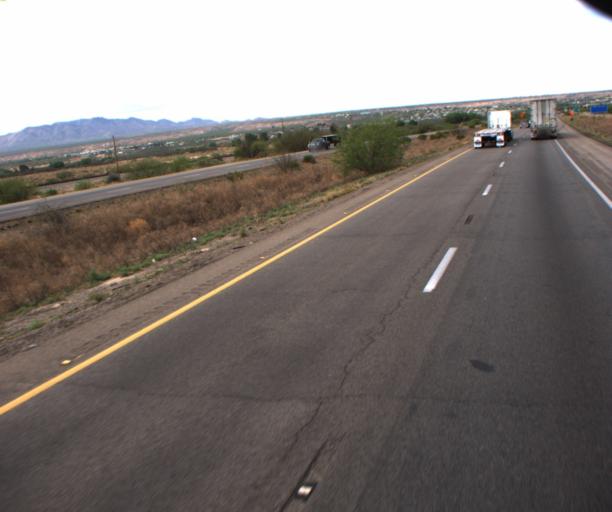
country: US
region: Arizona
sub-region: Cochise County
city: Benson
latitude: 31.9654
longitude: -110.2594
